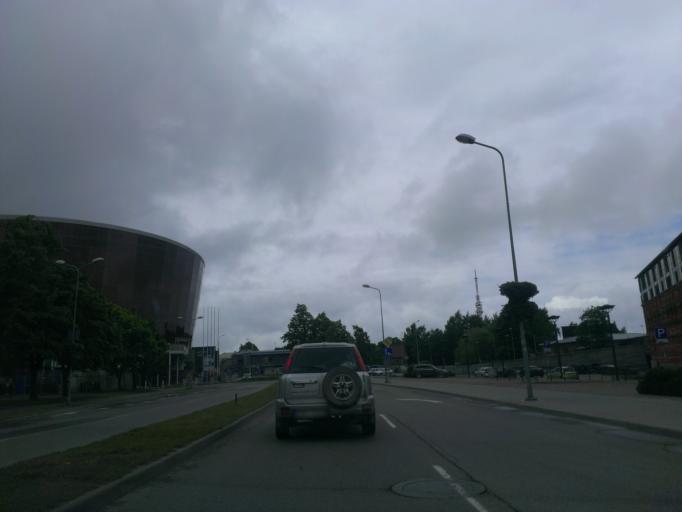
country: LV
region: Liepaja
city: Liepaja
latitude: 56.5121
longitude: 21.0123
